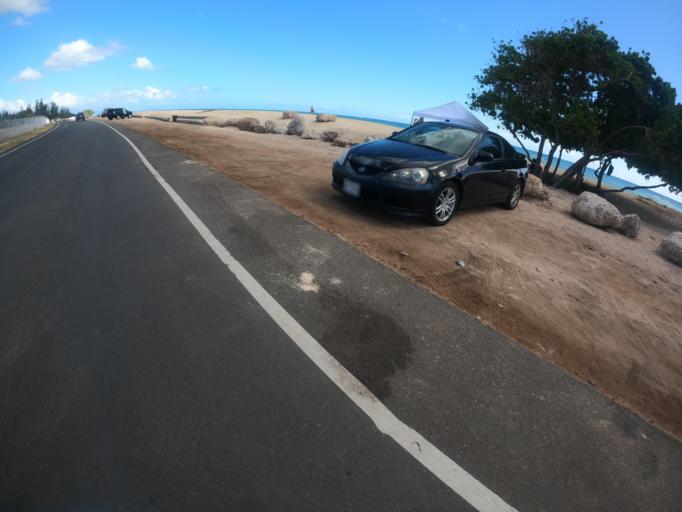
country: US
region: Hawaii
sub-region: Honolulu County
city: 'Ewa Villages
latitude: 21.3004
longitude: -158.0632
